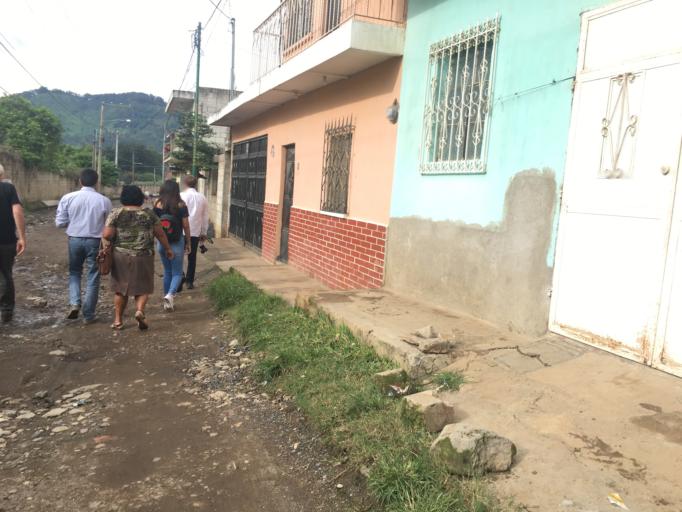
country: GT
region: Guatemala
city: Amatitlan
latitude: 14.4735
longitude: -90.6184
